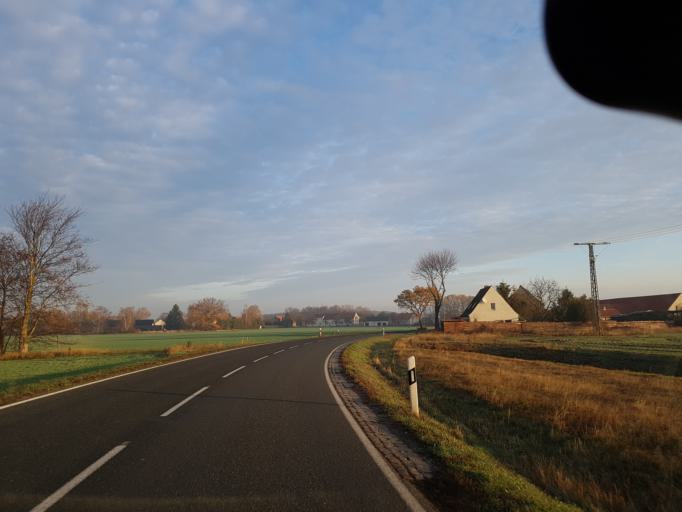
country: DE
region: Saxony-Anhalt
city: Elster
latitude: 51.8445
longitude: 12.8376
